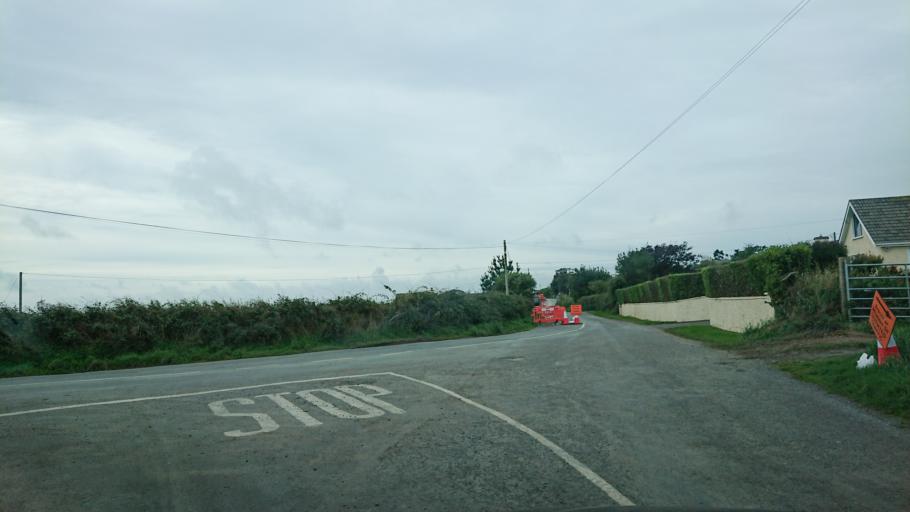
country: IE
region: Munster
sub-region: Waterford
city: Dunmore East
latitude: 52.1675
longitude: -6.9992
